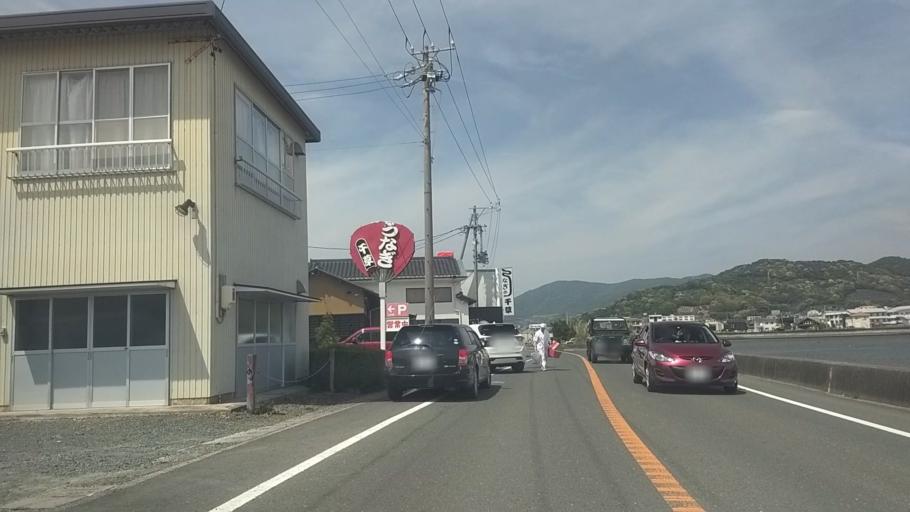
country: JP
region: Shizuoka
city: Kosai-shi
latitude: 34.7980
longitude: 137.5484
